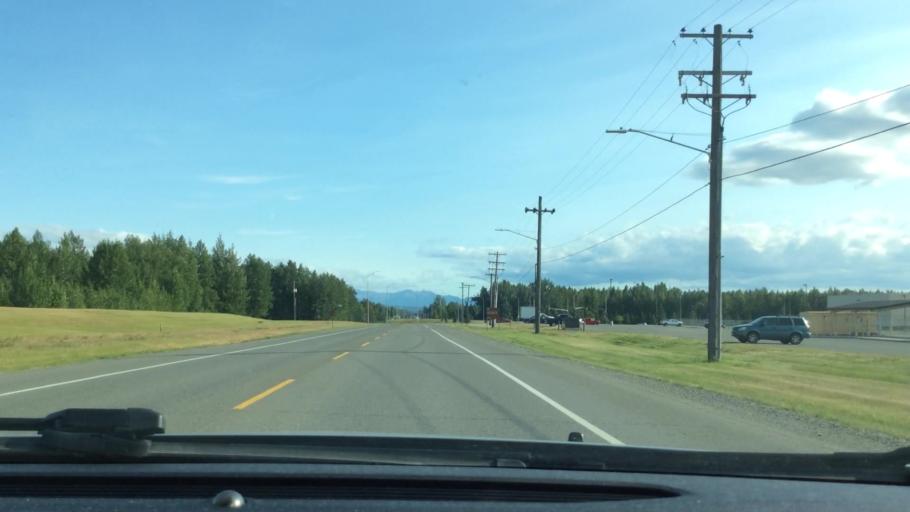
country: US
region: Alaska
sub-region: Anchorage Municipality
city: Anchorage
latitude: 61.2439
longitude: -149.7786
